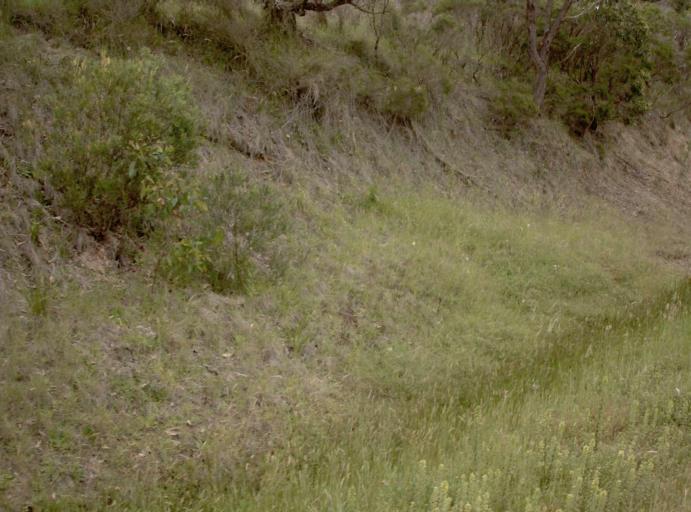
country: AU
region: Victoria
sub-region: Bass Coast
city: North Wonthaggi
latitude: -38.5404
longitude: 145.6979
